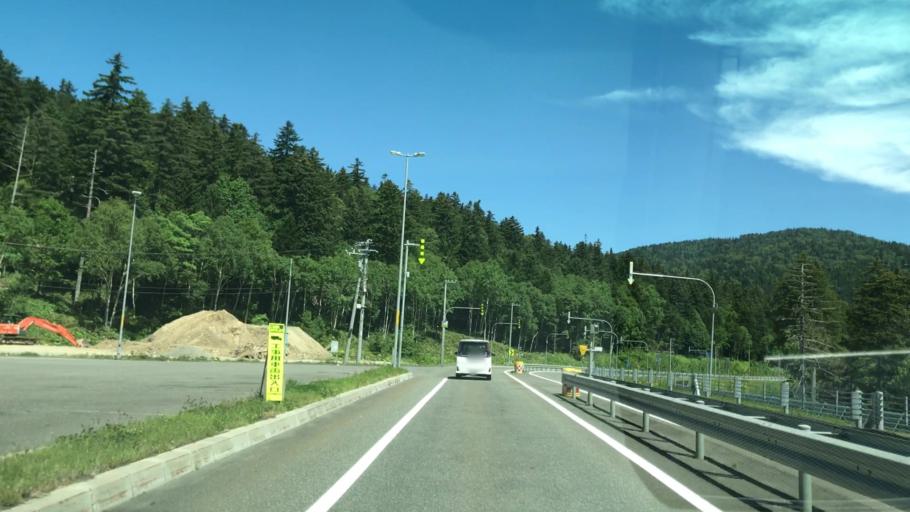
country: JP
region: Hokkaido
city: Shimo-furano
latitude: 42.9675
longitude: 142.6739
